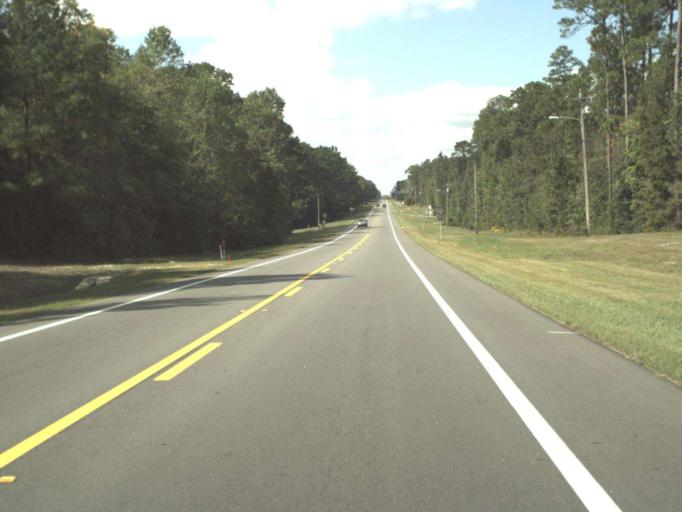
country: US
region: Florida
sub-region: Walton County
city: Freeport
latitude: 30.5011
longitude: -86.1433
